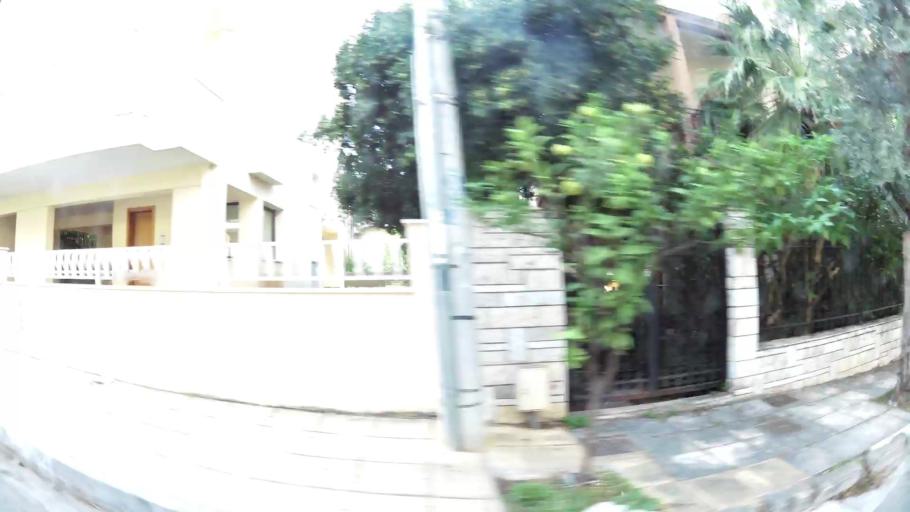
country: GR
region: Attica
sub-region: Nomarchia Athinas
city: Cholargos
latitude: 37.9958
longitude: 23.7975
